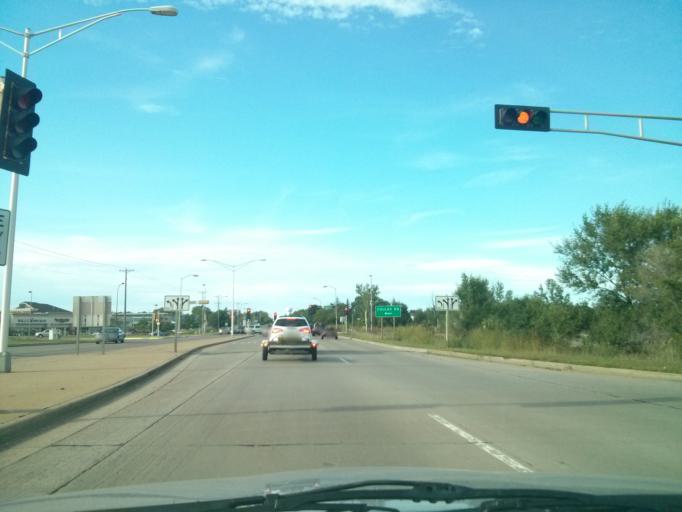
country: US
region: Wisconsin
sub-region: Saint Croix County
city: Hudson
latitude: 44.9642
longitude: -92.7211
